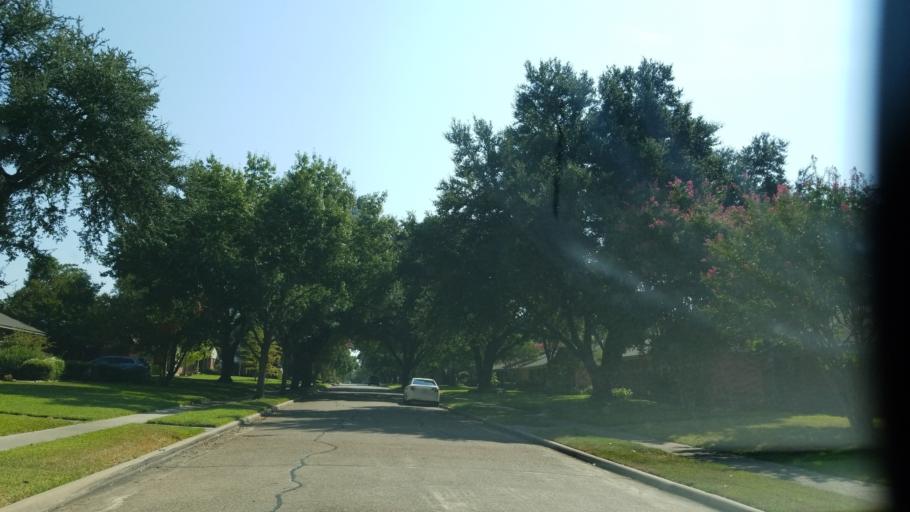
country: US
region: Texas
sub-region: Dallas County
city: Richardson
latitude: 32.9582
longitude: -96.7432
